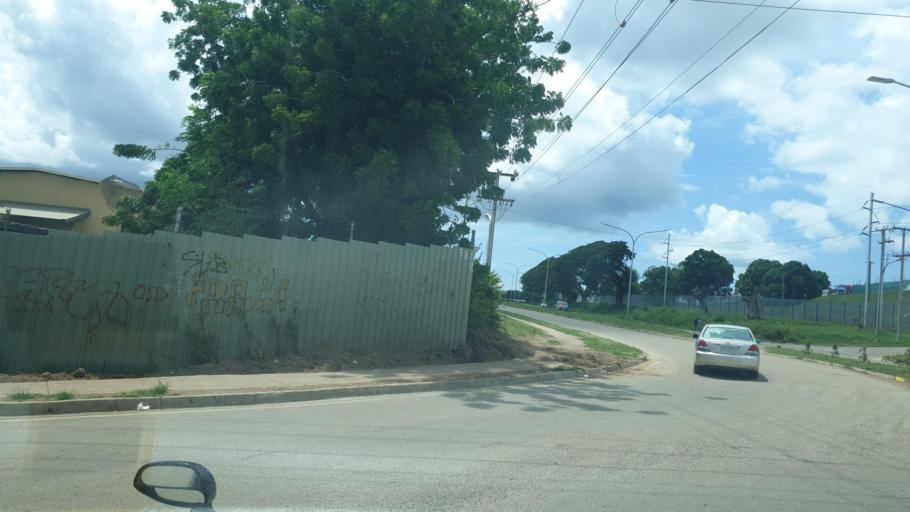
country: PG
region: National Capital
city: Port Moresby
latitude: -9.3796
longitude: 147.1555
